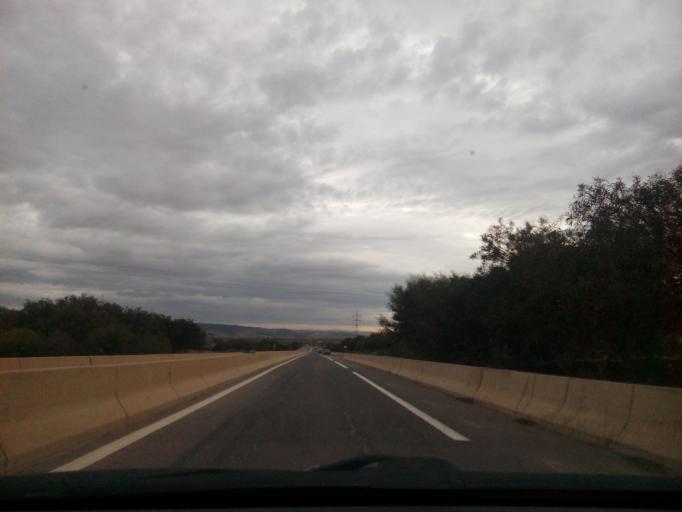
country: DZ
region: Oran
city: Sidi ech Chahmi
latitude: 35.5430
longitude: -0.3785
